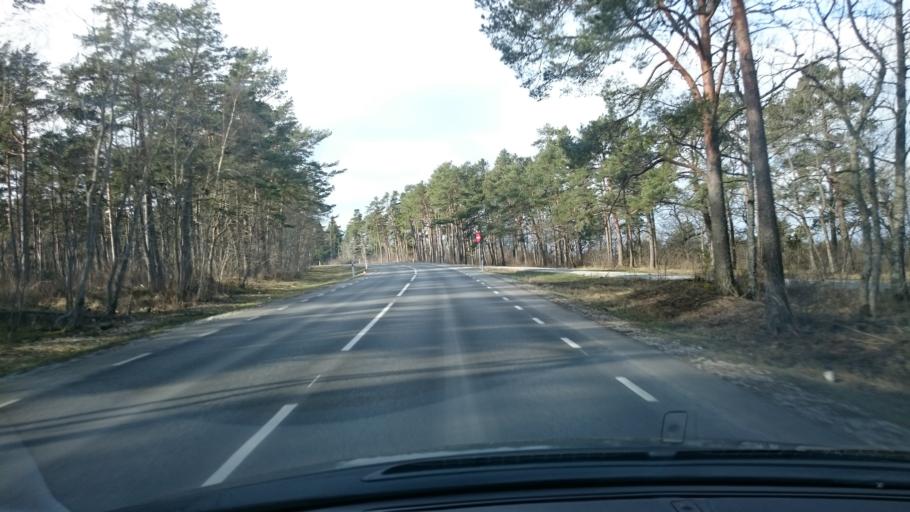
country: EE
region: Harju
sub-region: Keila linn
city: Keila
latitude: 59.3981
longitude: 24.2588
